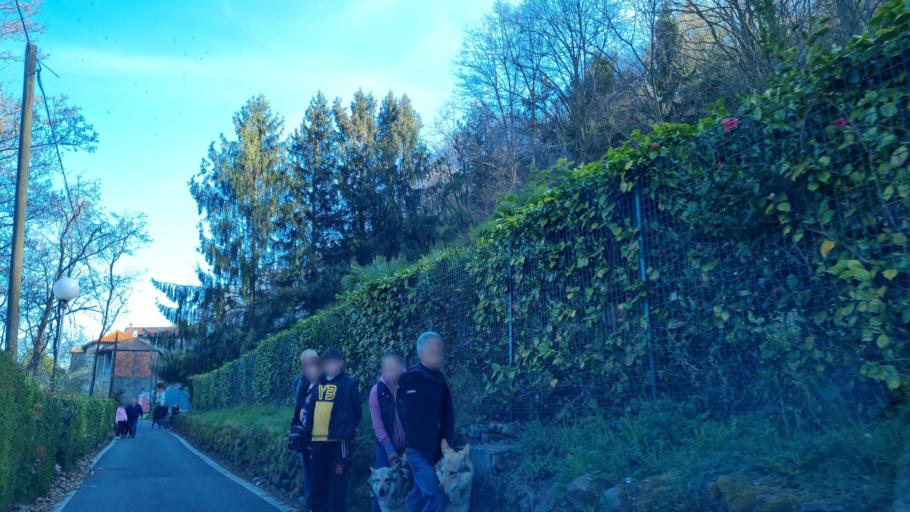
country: IT
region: Piedmont
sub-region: Provincia di Novara
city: San Maurizio D'Opaglio
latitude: 45.7768
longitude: 8.4083
